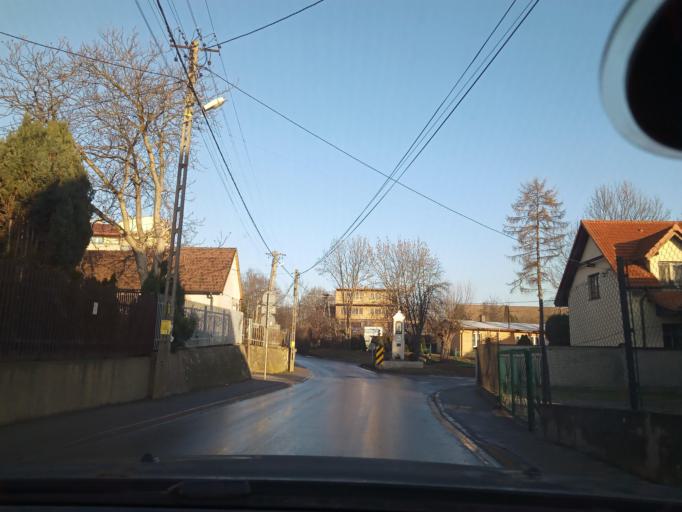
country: PL
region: Lesser Poland Voivodeship
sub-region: Powiat krakowski
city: Michalowice
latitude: 50.0977
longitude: 20.0255
